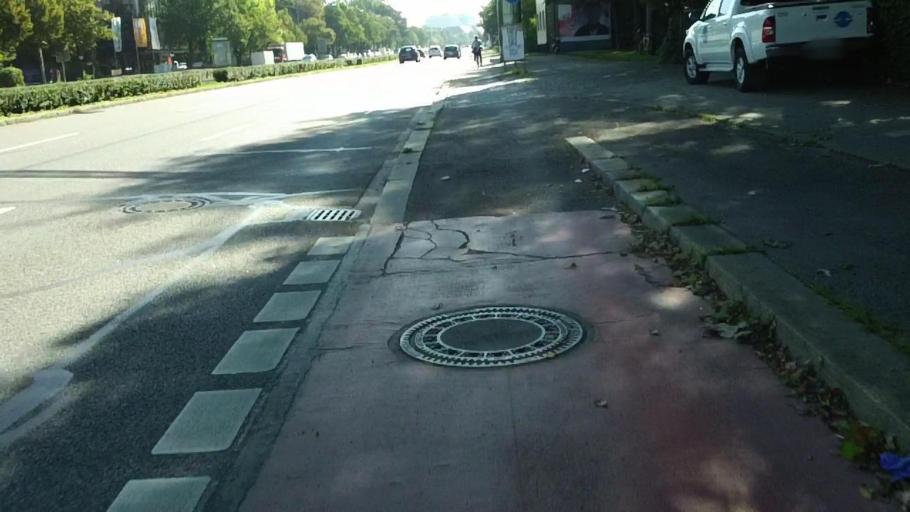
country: DE
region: Bavaria
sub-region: Upper Bavaria
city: Munich
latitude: 48.1752
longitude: 11.5229
